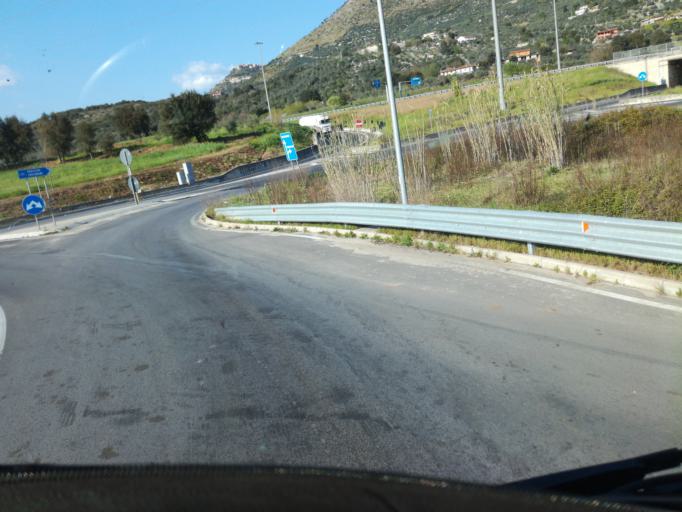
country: IT
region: Latium
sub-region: Provincia di Latina
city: Roccasecca dei Volsci
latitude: 41.4577
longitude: 13.2035
